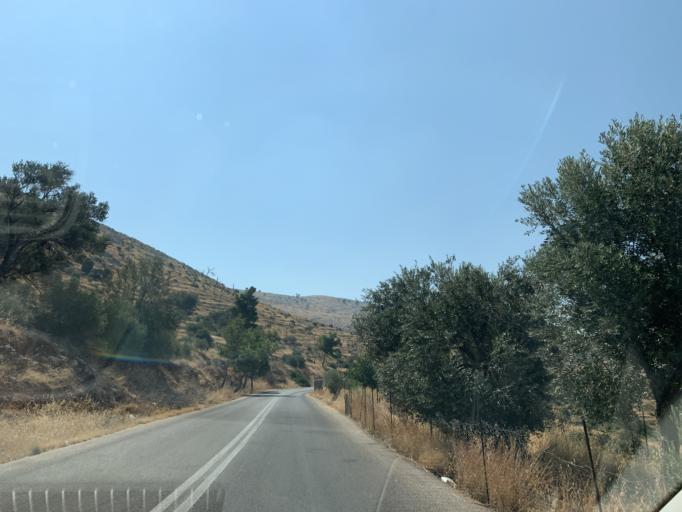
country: GR
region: North Aegean
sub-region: Chios
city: Thymiana
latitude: 38.3233
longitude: 26.0043
